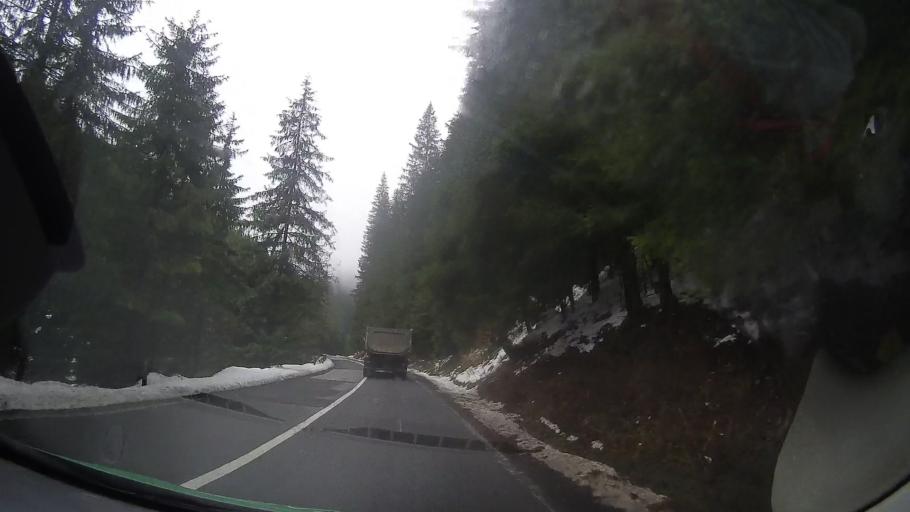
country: RO
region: Neamt
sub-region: Comuna Bicaz Chei
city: Bicaz Chei
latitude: 46.7807
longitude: 25.7507
